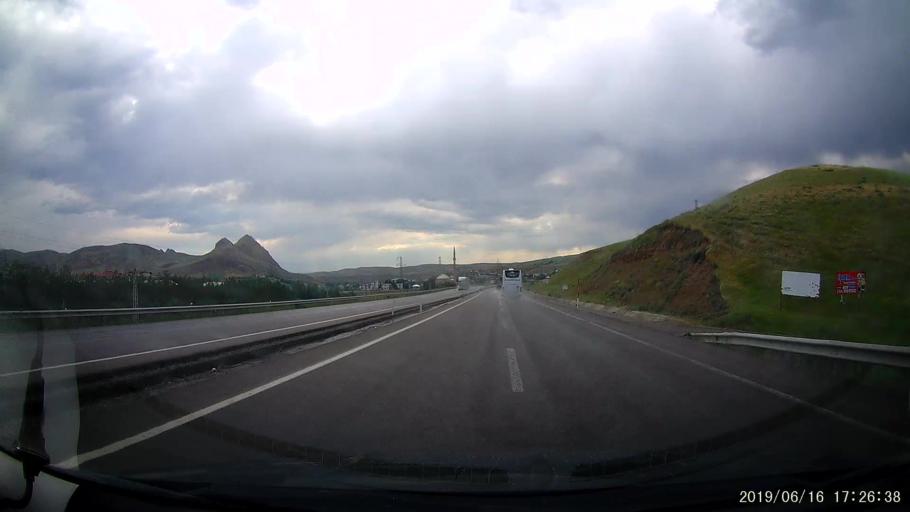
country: TR
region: Erzincan
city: Tercan
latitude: 39.7697
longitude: 40.4082
